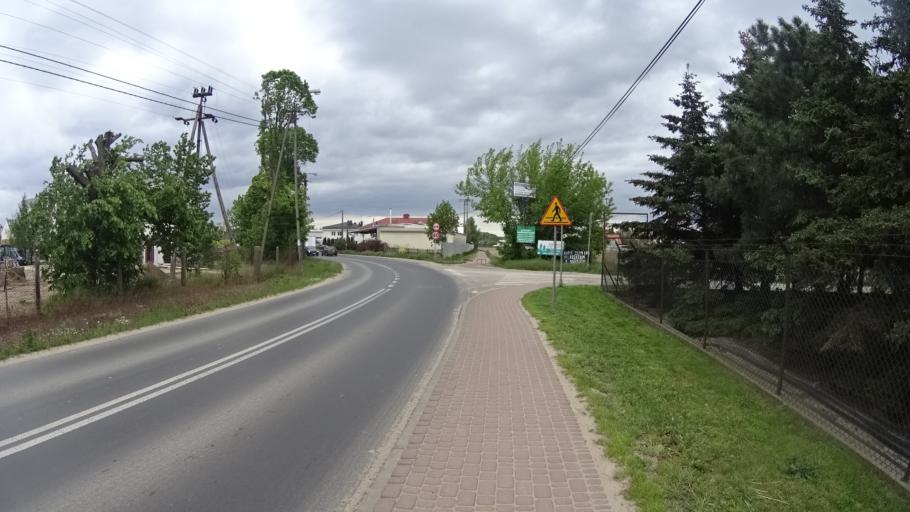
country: PL
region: Masovian Voivodeship
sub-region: Powiat warszawski zachodni
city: Babice
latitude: 52.2445
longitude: 20.8487
